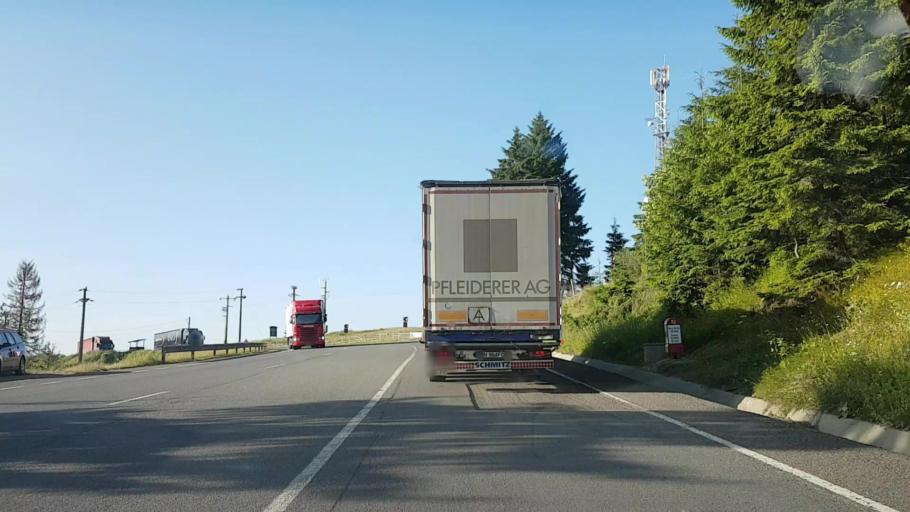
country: RO
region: Bistrita-Nasaud
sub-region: Comuna Lunca Ilvei
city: Lunca Ilvei
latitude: 47.2650
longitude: 25.0200
